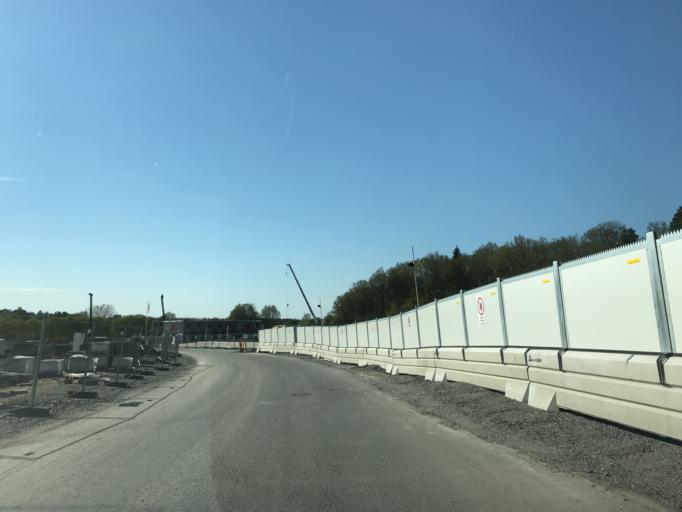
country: SE
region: Stockholm
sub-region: Huddinge Kommun
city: Huddinge
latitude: 59.2822
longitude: 18.0026
